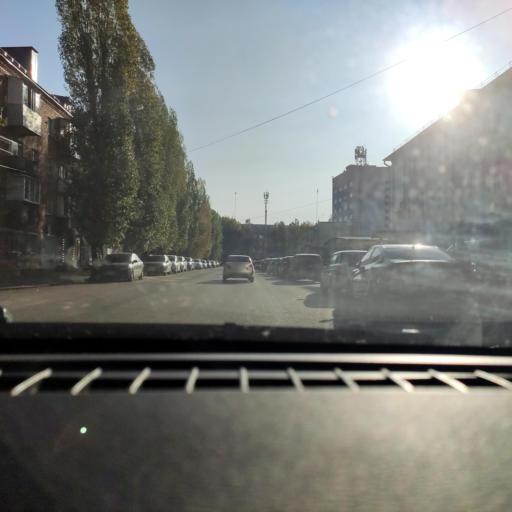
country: RU
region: Voronezj
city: Voronezh
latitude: 51.6804
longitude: 39.2572
